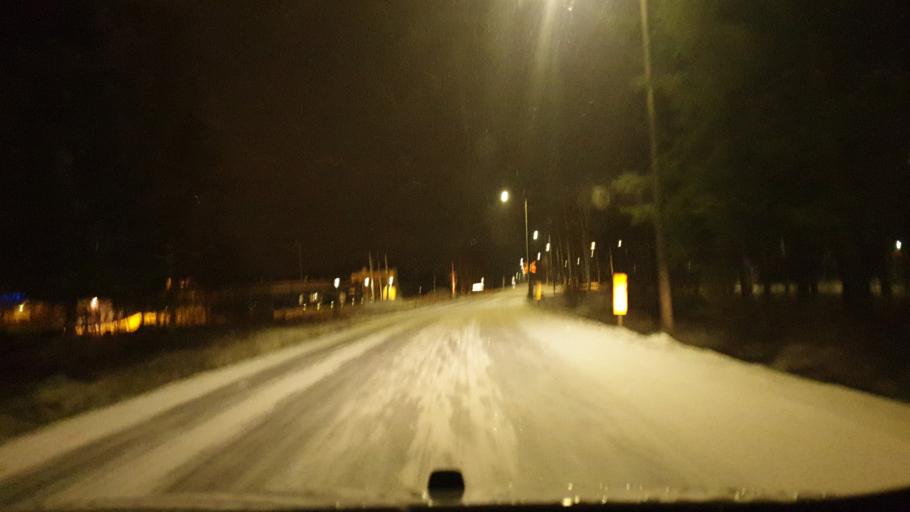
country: FI
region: Northern Ostrobothnia
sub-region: Oulu
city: Oulu
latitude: 64.9932
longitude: 25.4480
